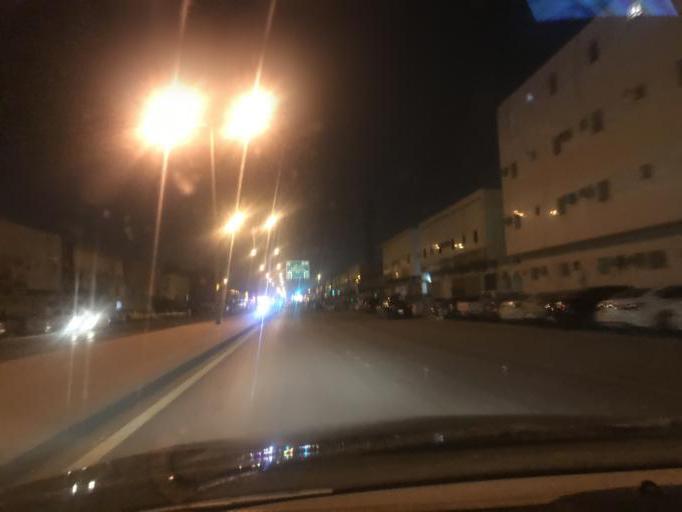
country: SA
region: Ar Riyad
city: Riyadh
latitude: 24.7643
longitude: 46.7964
